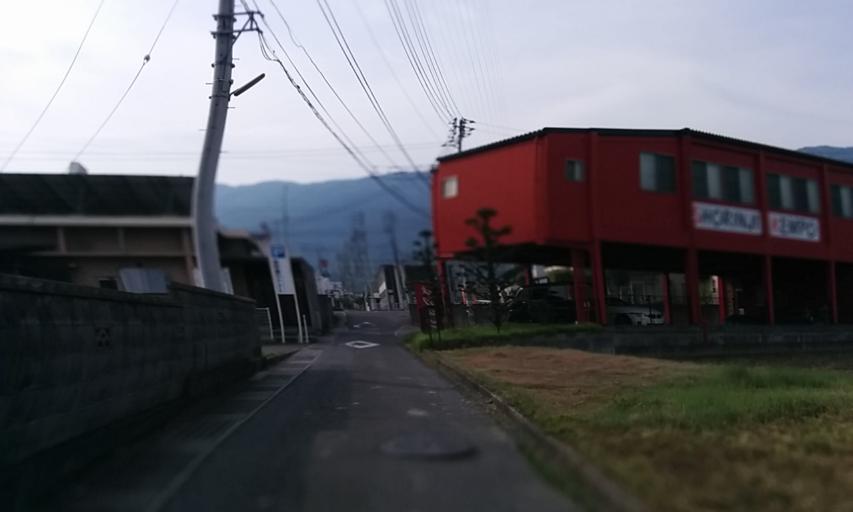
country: JP
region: Ehime
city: Kawanoecho
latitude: 33.9828
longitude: 133.5554
